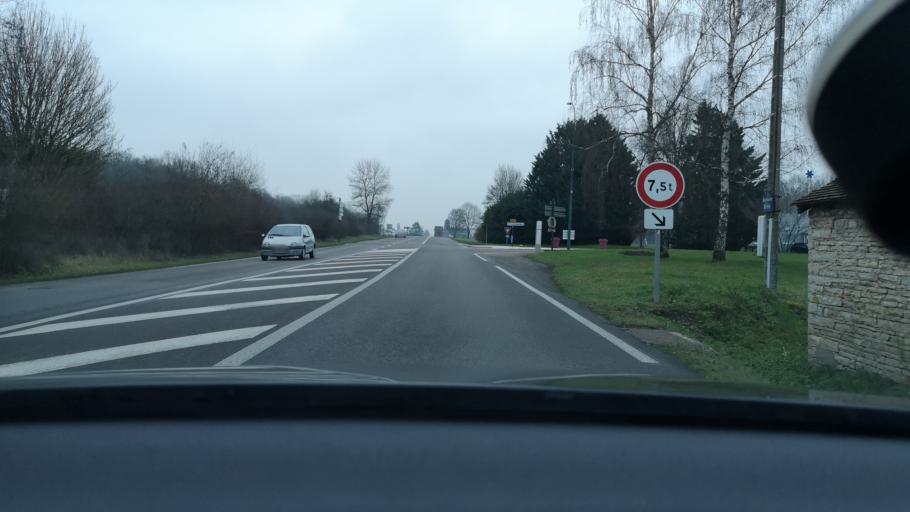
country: FR
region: Bourgogne
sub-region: Departement de Saone-et-Loire
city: Dracy-le-Fort
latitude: 46.8019
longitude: 4.7833
